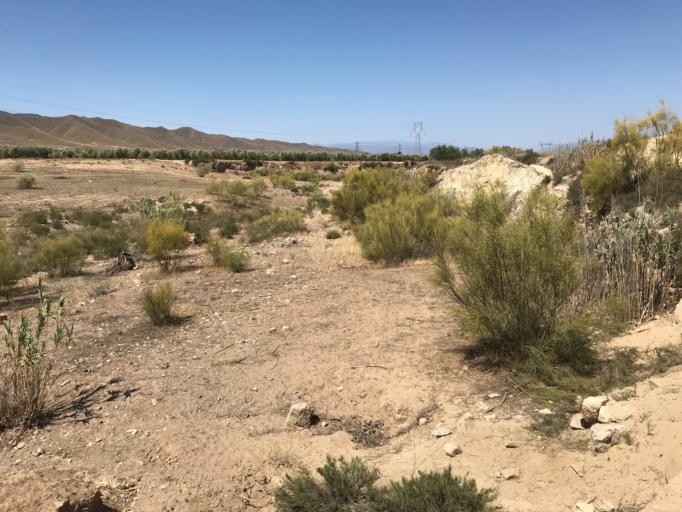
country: ES
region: Andalusia
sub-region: Provincia de Almeria
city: Turrillas
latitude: 37.0746
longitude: -2.2965
